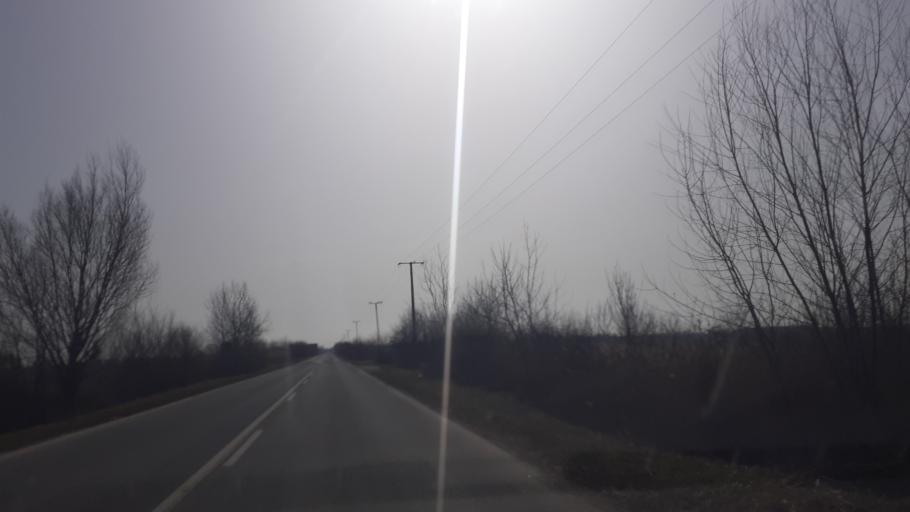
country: HU
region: Pest
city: Bugyi
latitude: 47.2116
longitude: 19.1487
